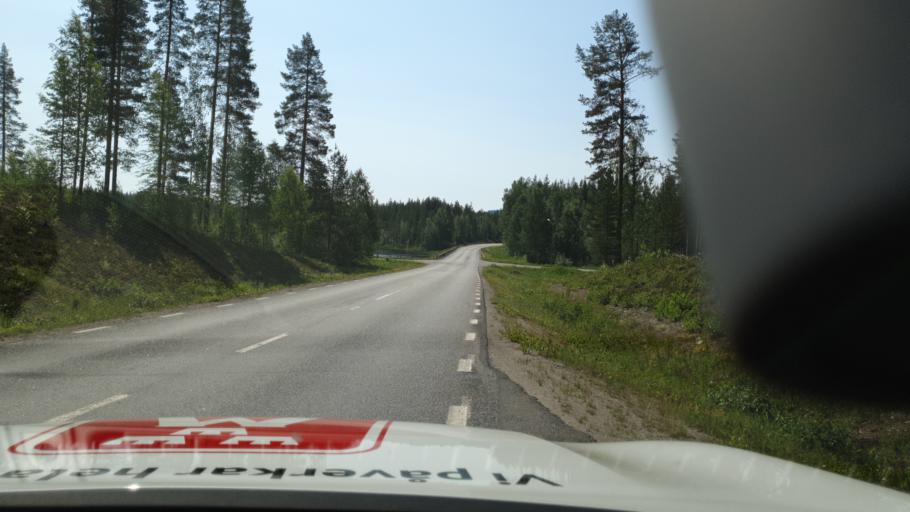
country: SE
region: Vaesterbotten
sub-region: Norsjo Kommun
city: Norsjoe
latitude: 64.9720
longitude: 19.7163
